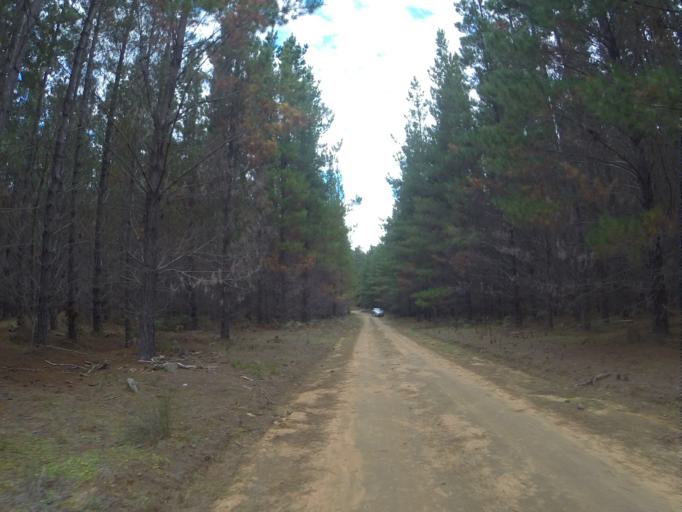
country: AU
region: New South Wales
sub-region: Wingecarribee
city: Moss Vale
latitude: -34.5229
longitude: 150.2353
